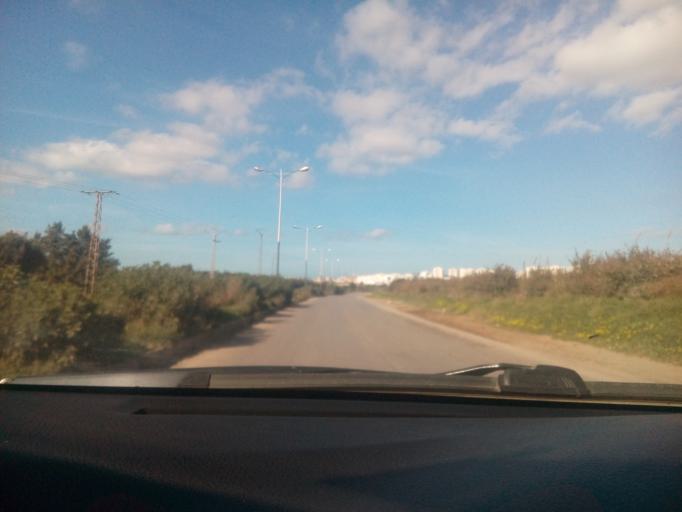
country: DZ
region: Oran
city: Bir el Djir
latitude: 35.6845
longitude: -0.5720
